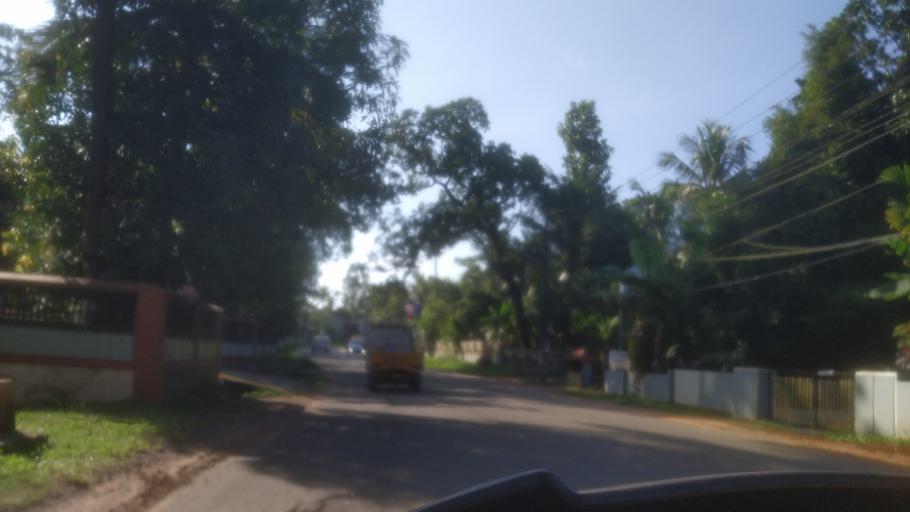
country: IN
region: Kerala
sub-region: Ernakulam
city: Muvattupuzha
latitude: 9.9792
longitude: 76.5232
